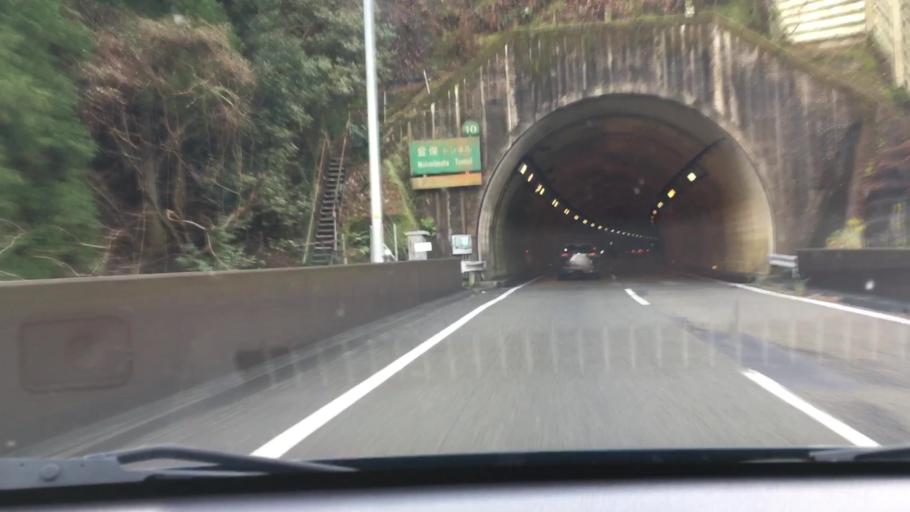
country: JP
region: Kumamoto
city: Yatsushiro
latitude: 32.4242
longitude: 130.7017
